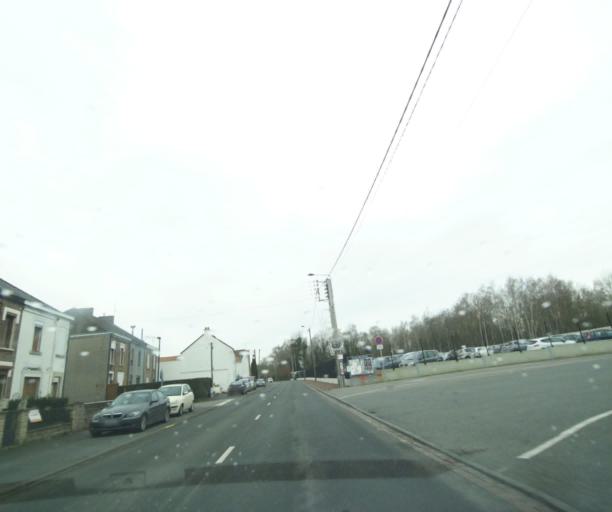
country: FR
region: Nord-Pas-de-Calais
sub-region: Departement du Nord
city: Quievrechain
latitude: 50.3873
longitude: 3.6606
